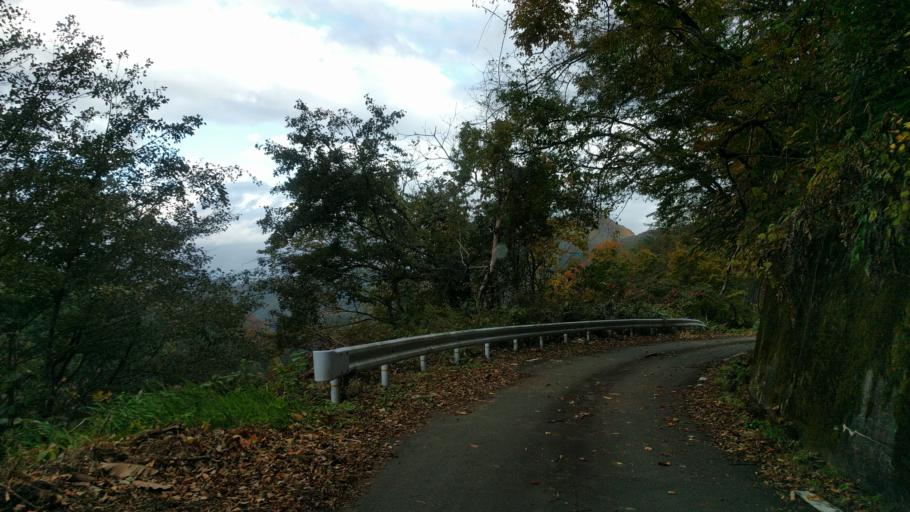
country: JP
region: Fukushima
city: Kitakata
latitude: 37.3930
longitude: 139.7139
